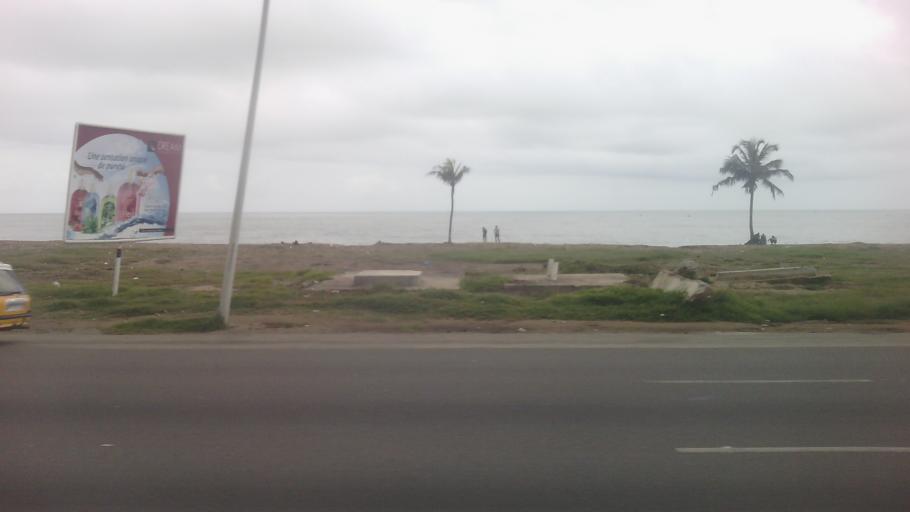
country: CI
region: Lagunes
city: Abidjan
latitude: 5.2479
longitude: -3.9503
